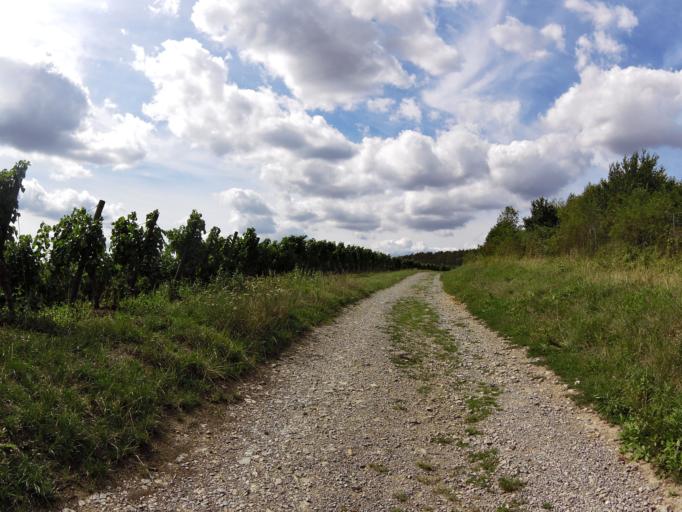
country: DE
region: Bavaria
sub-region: Regierungsbezirk Unterfranken
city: Erlabrunn
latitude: 49.8467
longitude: 9.8423
